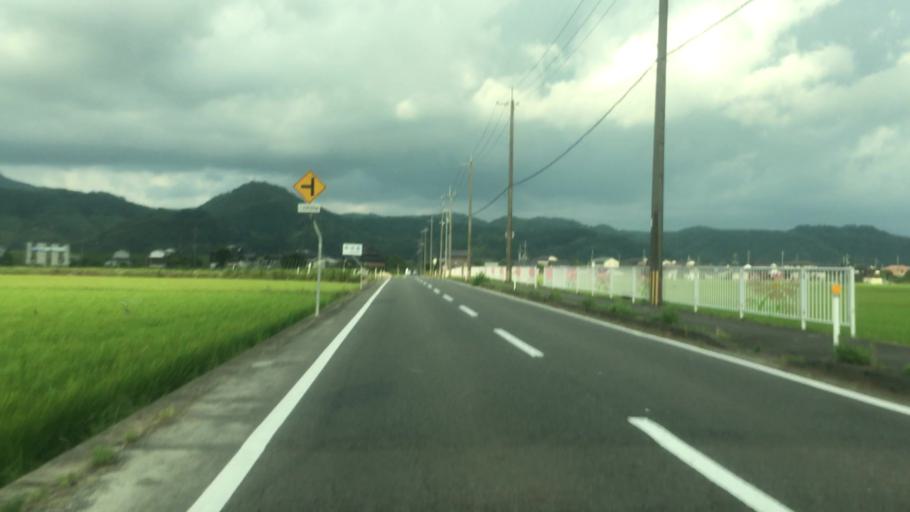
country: JP
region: Hyogo
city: Toyooka
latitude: 35.5647
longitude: 134.8069
